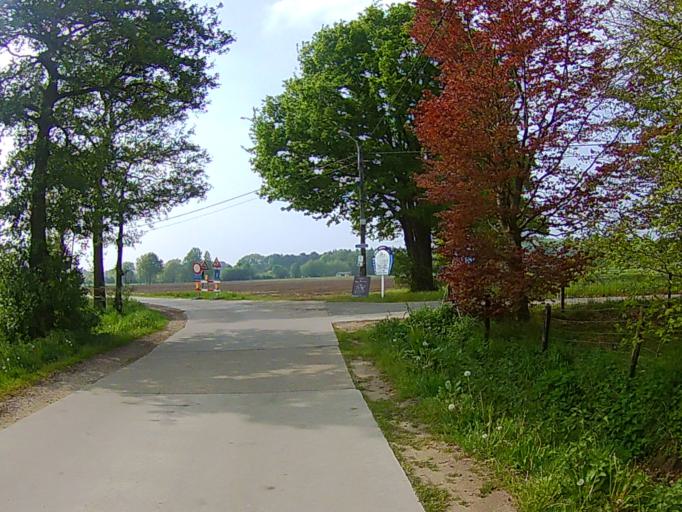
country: BE
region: Flanders
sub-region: Provincie Antwerpen
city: Grobbendonk
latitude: 51.2068
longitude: 4.7274
